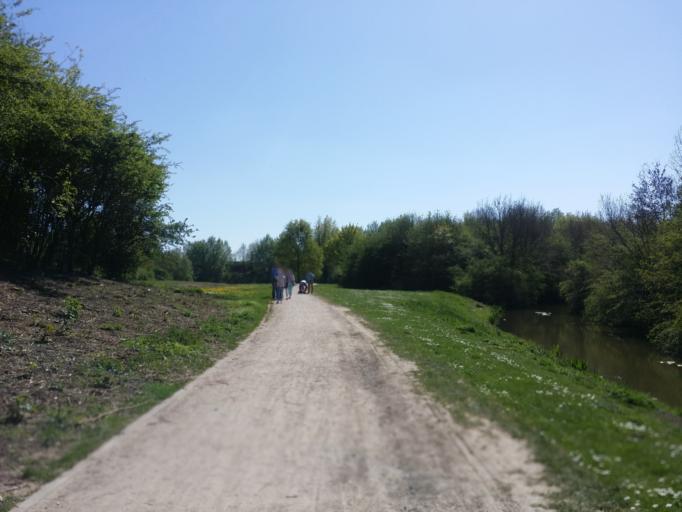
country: DE
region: Bremen
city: Bremen
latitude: 53.0267
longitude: 8.8296
